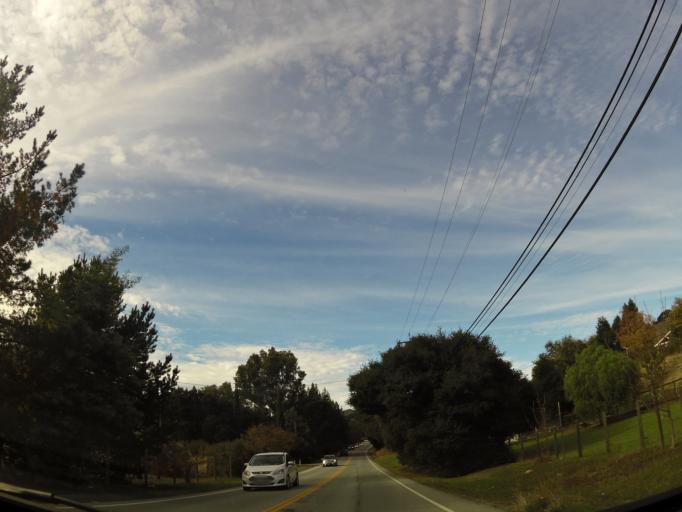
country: US
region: California
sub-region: Santa Clara County
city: San Martin
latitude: 37.0516
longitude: -121.6576
